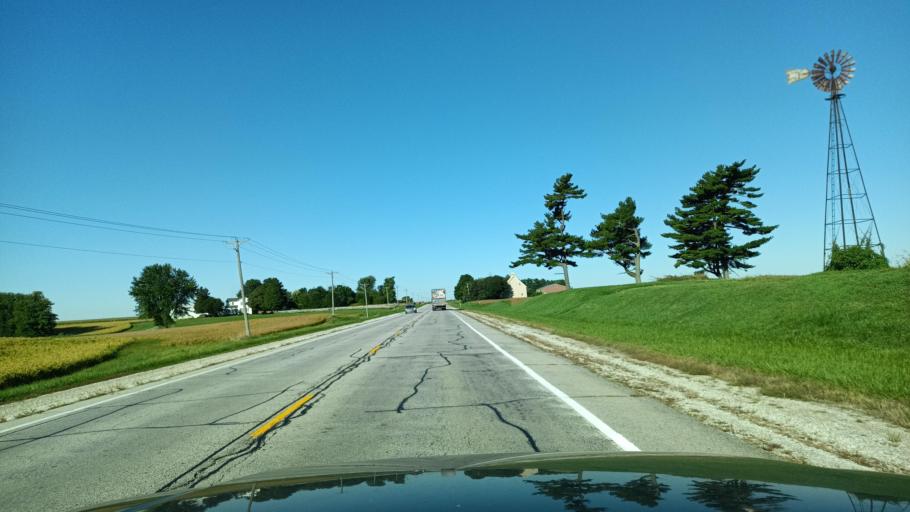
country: US
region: Illinois
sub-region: Warren County
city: Monmouth
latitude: 40.8785
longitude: -90.7079
